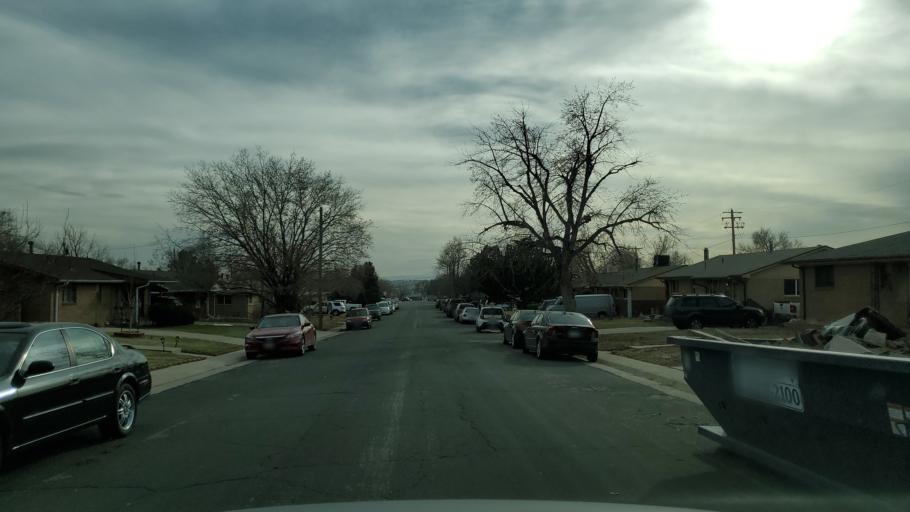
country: US
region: Colorado
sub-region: Adams County
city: Westminster
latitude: 39.8326
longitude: -105.0234
